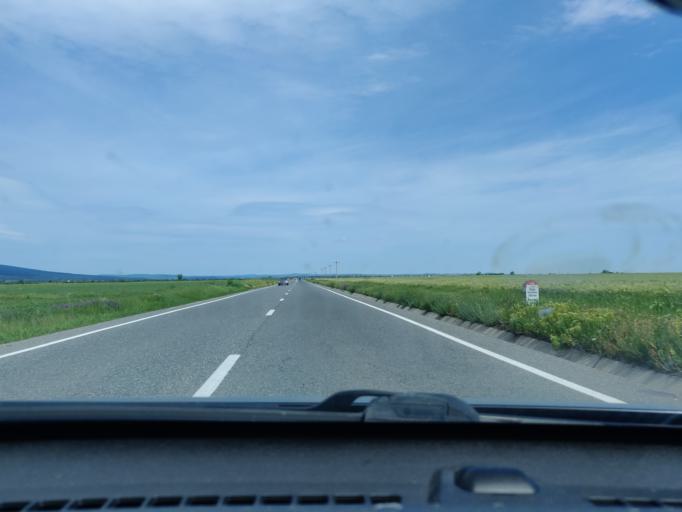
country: RO
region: Vrancea
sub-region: Oras Odobesti
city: Unirea
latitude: 45.7839
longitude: 27.1144
